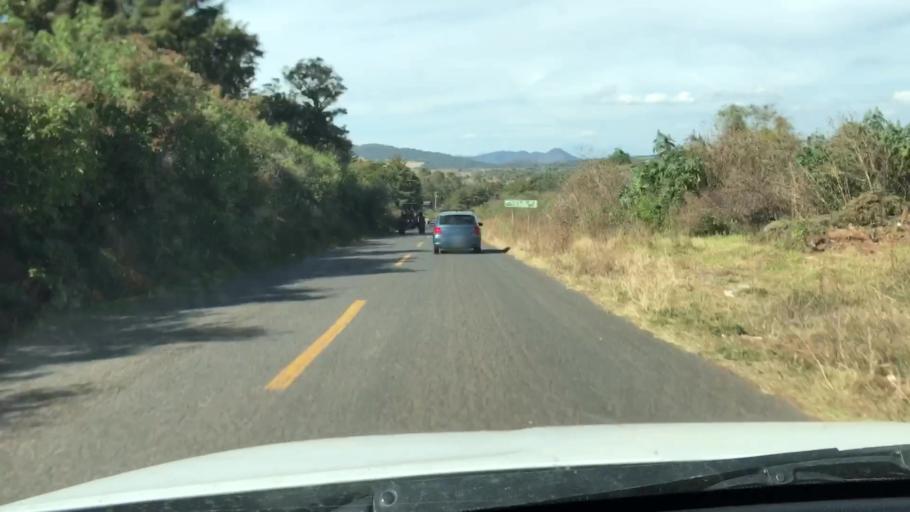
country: MX
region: Jalisco
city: Chiquilistlan
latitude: 20.1456
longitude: -103.7239
